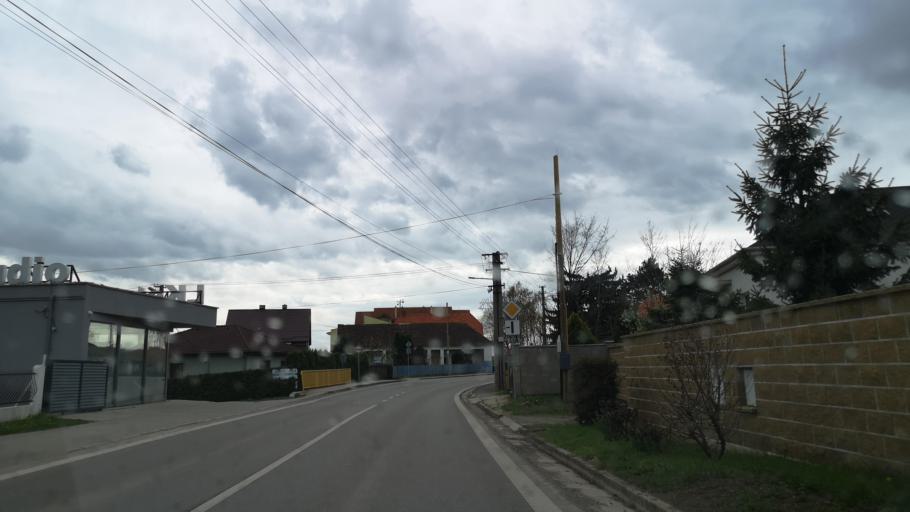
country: SK
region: Nitriansky
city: Zlate Moravce
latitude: 48.3375
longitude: 18.3565
